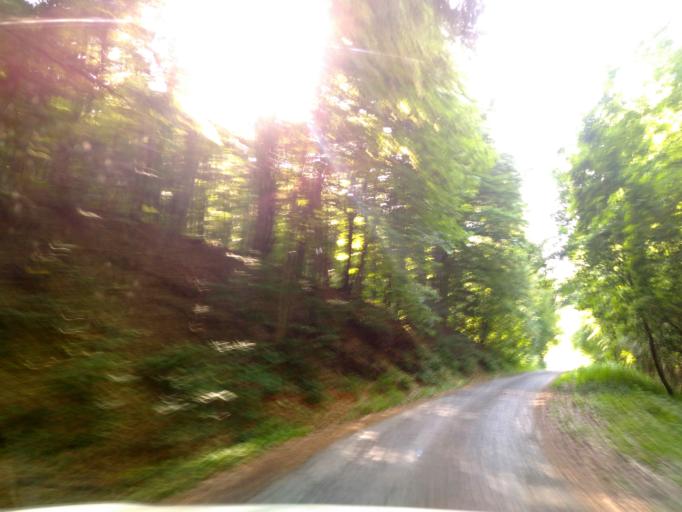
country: HU
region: Baranya
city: Hosszuheteny
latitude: 46.2228
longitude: 18.3409
